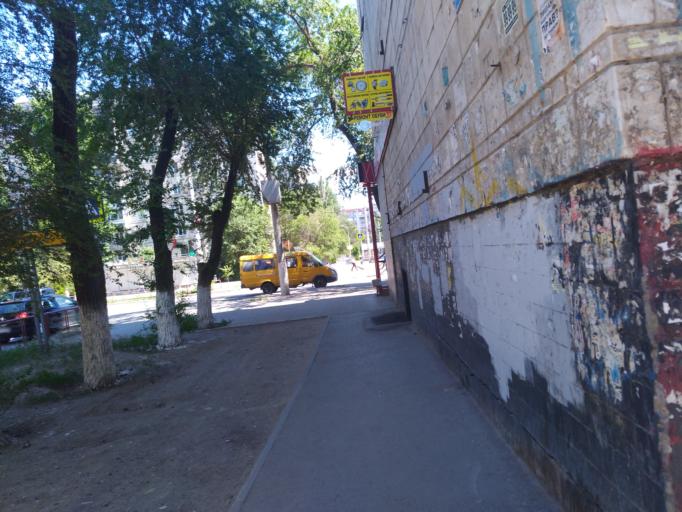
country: RU
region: Volgograd
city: Volgograd
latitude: 48.6780
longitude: 44.4734
